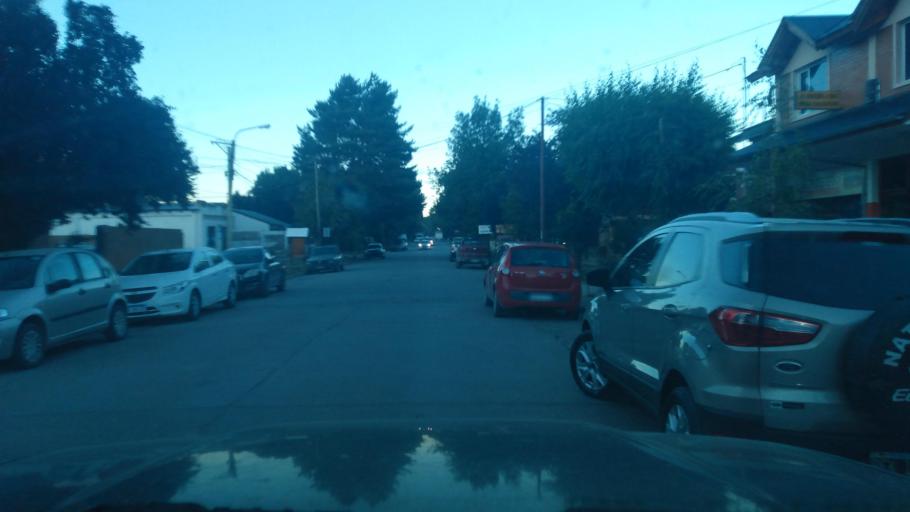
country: AR
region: Neuquen
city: Junin de los Andes
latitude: -39.9496
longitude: -71.0725
